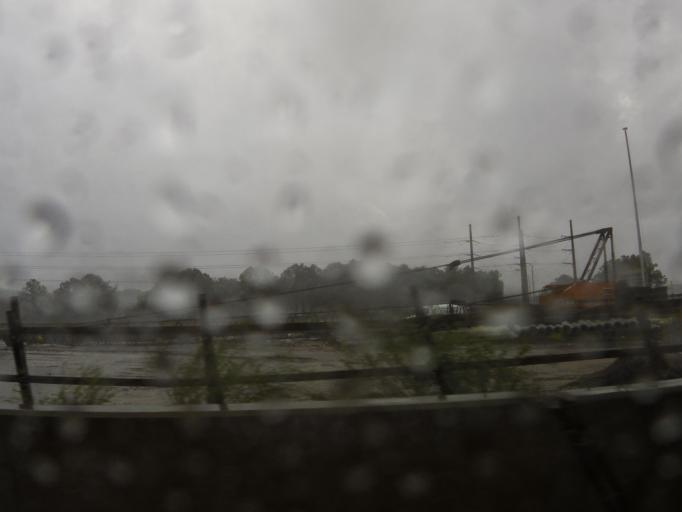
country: US
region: Florida
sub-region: Duval County
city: Baldwin
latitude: 30.2896
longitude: -81.9783
